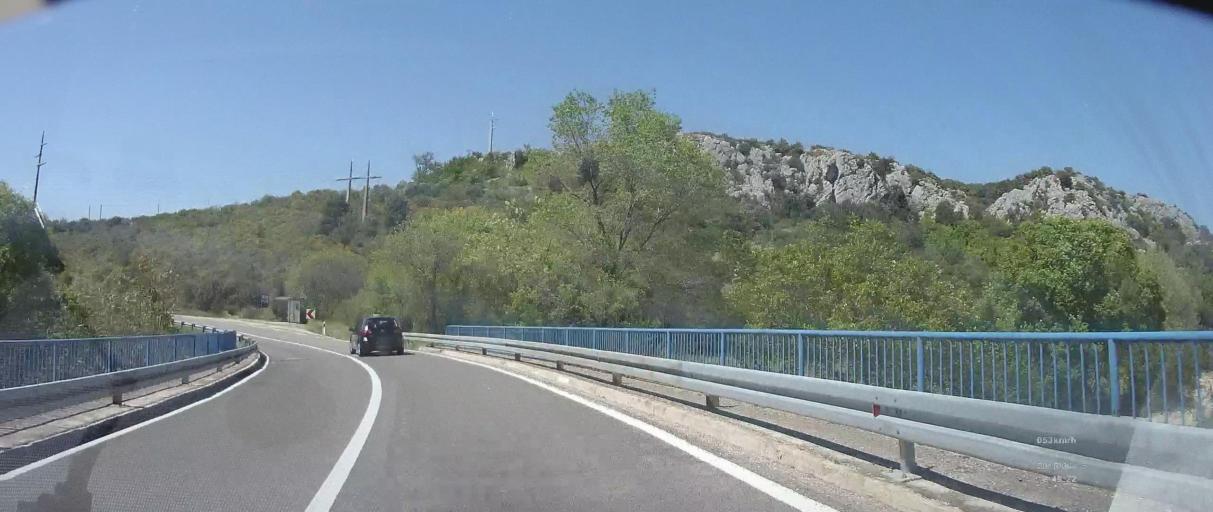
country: HR
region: Sibensko-Kniniska
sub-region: Grad Sibenik
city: Brodarica
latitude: 43.6744
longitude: 16.0271
